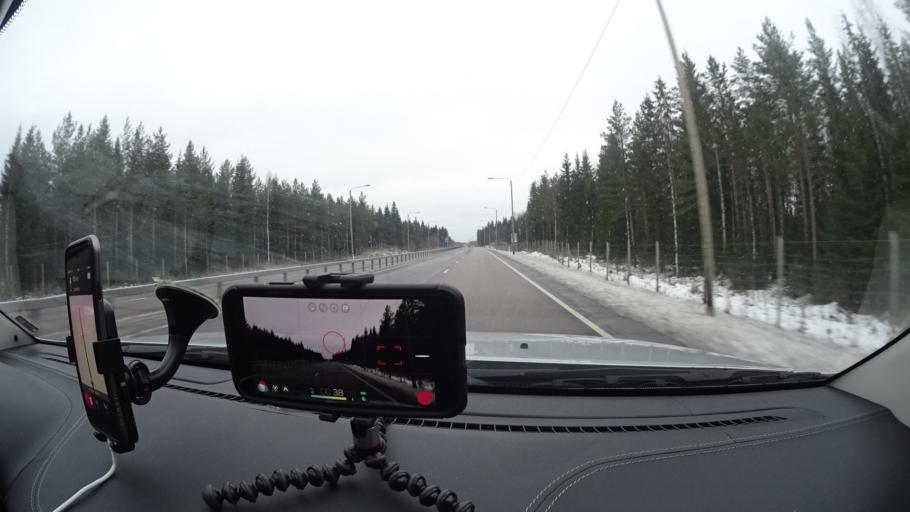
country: FI
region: Paijanne Tavastia
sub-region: Lahti
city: Hartola
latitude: 61.4764
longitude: 25.9809
